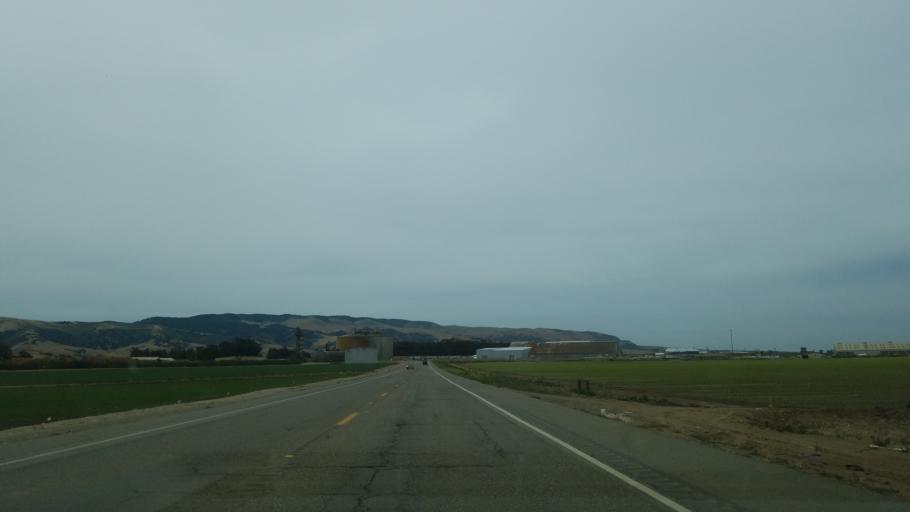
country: US
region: California
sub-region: Santa Barbara County
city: Santa Maria
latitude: 34.9192
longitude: -120.5079
